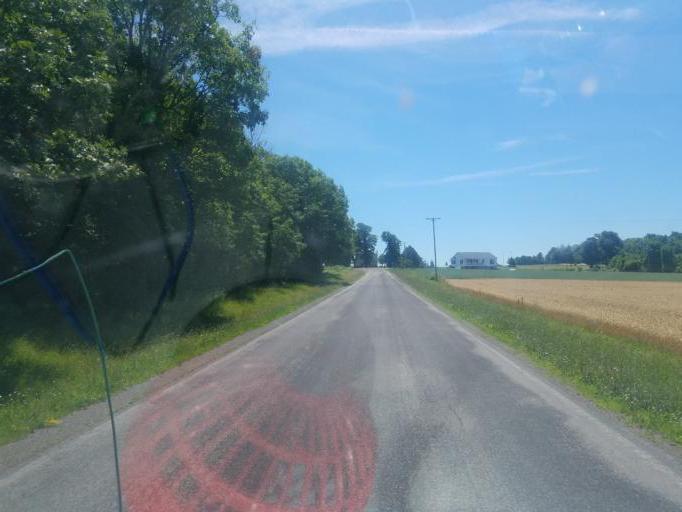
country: US
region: New York
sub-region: Yates County
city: Penn Yan
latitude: 42.6346
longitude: -77.0158
